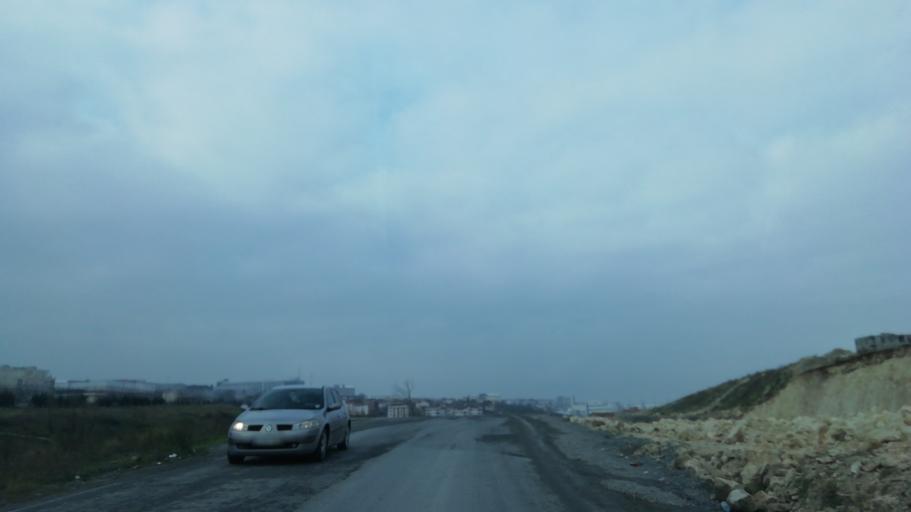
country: TR
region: Istanbul
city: Esenyurt
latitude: 41.1108
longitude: 28.6496
